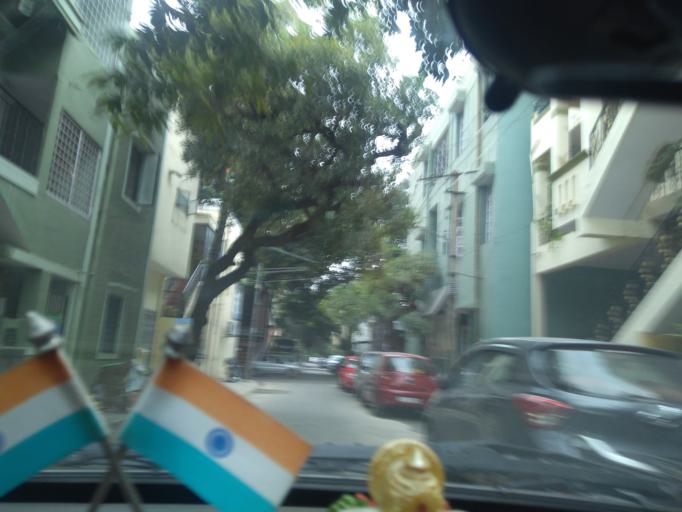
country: IN
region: Karnataka
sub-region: Bangalore Urban
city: Bangalore
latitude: 12.9873
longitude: 77.5517
